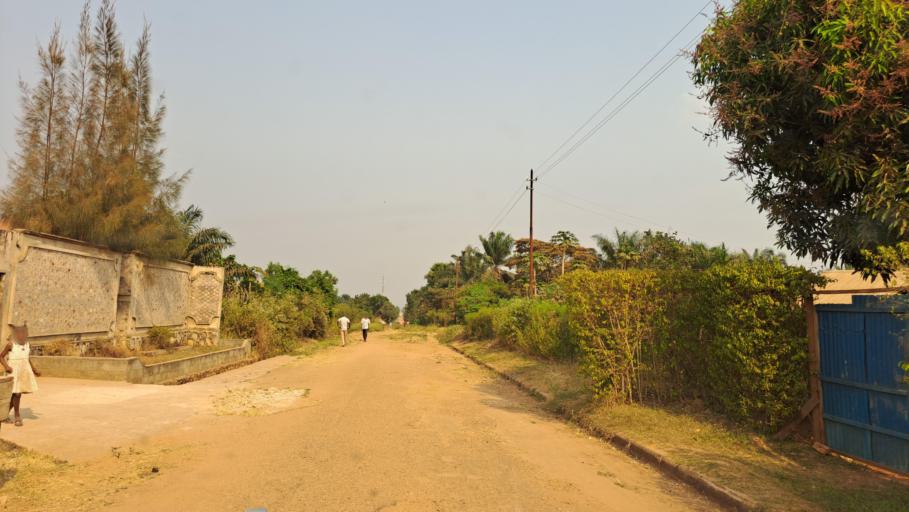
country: CD
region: Kasai-Oriental
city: Mbuji-Mayi
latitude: -6.1342
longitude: 23.5877
